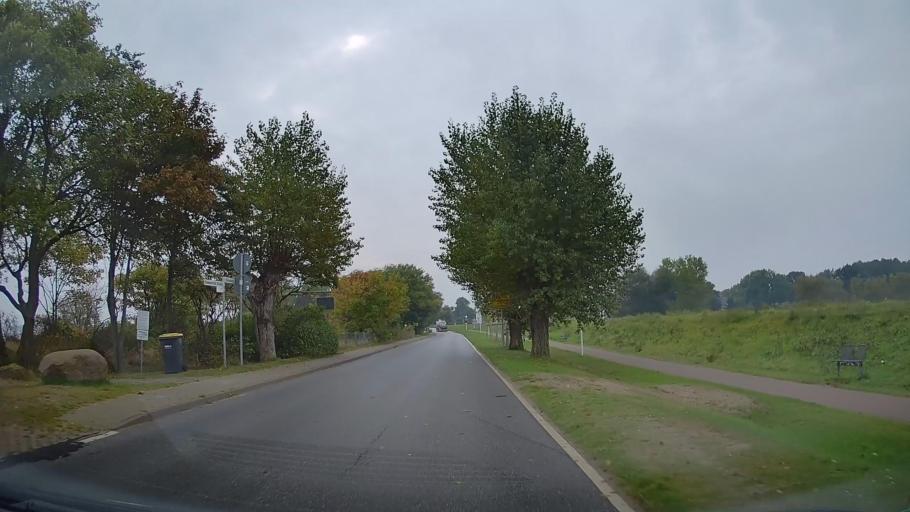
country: DE
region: Mecklenburg-Vorpommern
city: Ostseebad Boltenhagen
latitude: 53.9964
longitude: 11.1960
